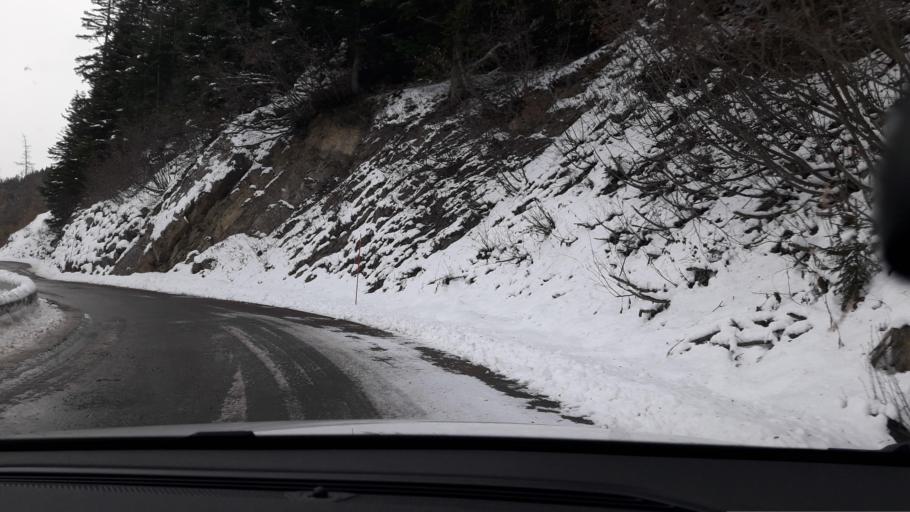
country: FR
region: Rhone-Alpes
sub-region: Departement de la Savoie
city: Saint-Michel-de-Maurienne
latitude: 45.2242
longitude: 6.4121
